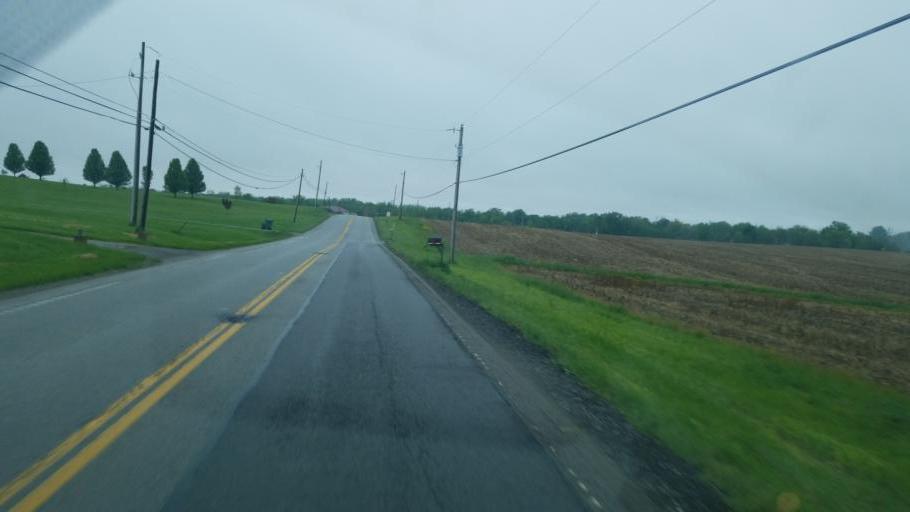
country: US
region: Ohio
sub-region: Highland County
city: Hillsboro
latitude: 39.2776
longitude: -83.5937
